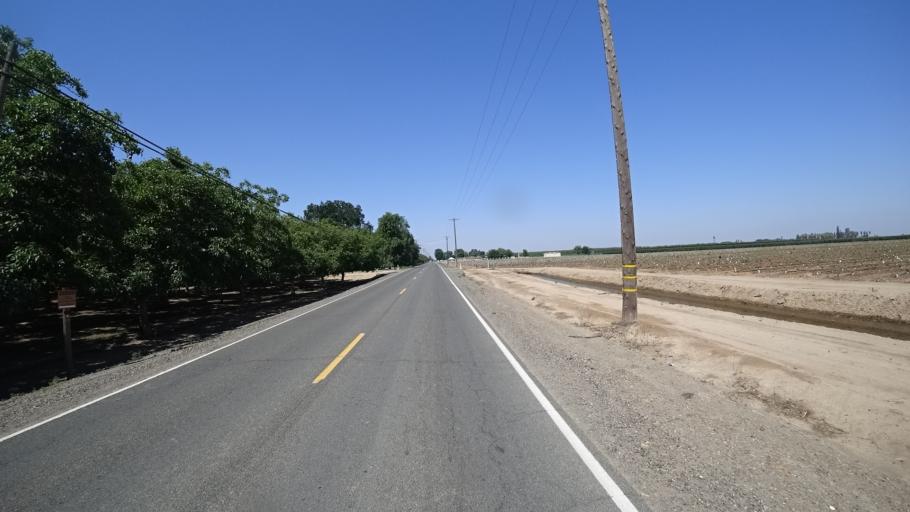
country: US
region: California
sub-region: Kings County
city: Lucerne
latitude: 36.3718
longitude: -119.6660
